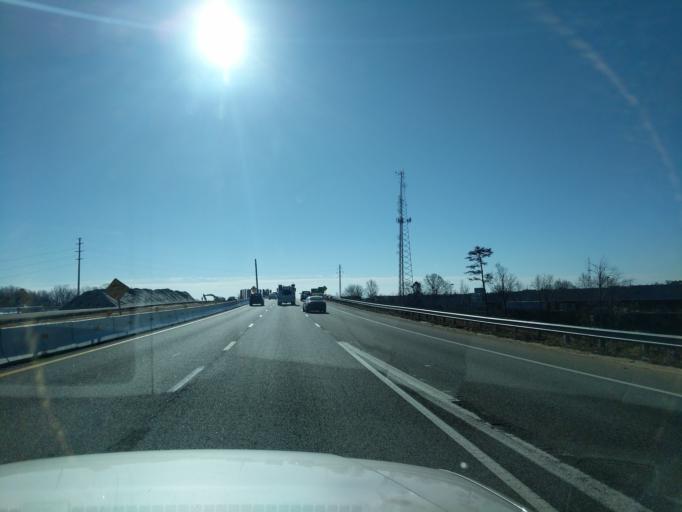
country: US
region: South Carolina
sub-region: Greenville County
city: Mauldin
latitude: 34.8300
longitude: -82.2945
